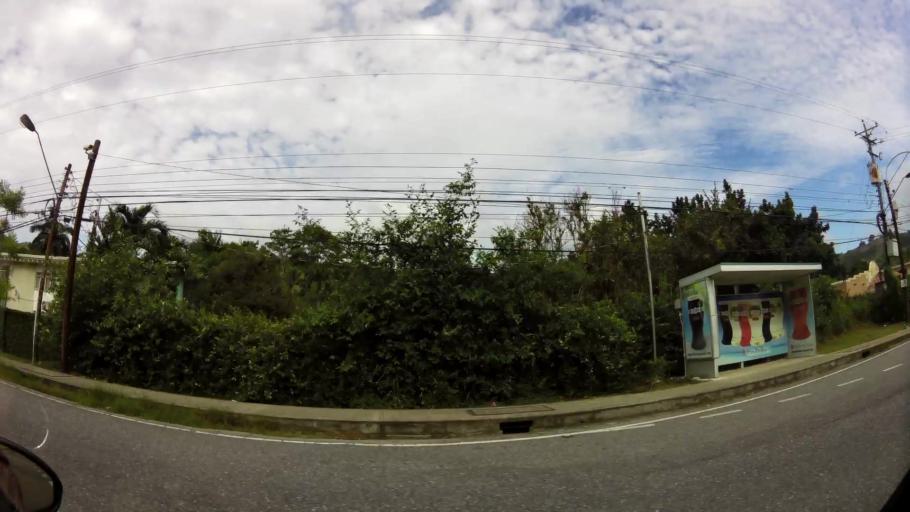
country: TT
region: Diego Martin
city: Petit Valley
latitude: 10.7130
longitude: -61.5064
